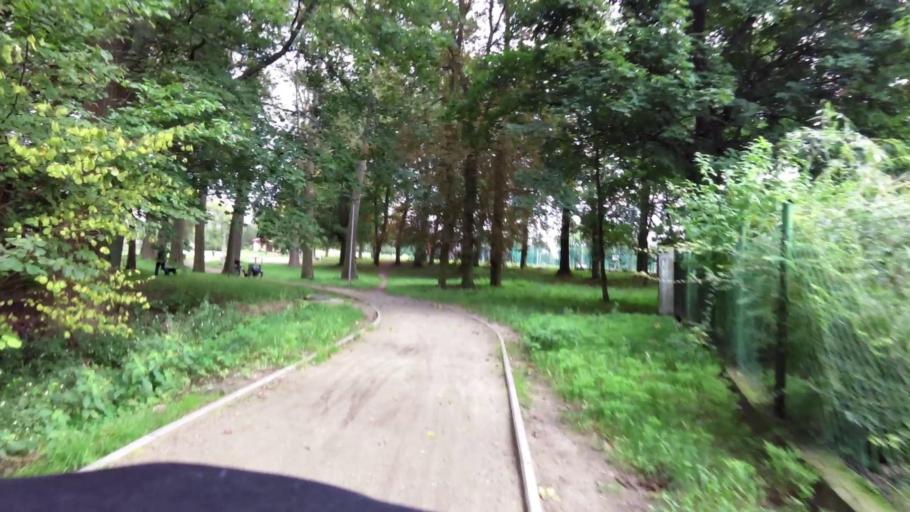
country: PL
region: West Pomeranian Voivodeship
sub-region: Powiat stargardzki
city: Marianowo
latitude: 53.3782
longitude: 15.2676
